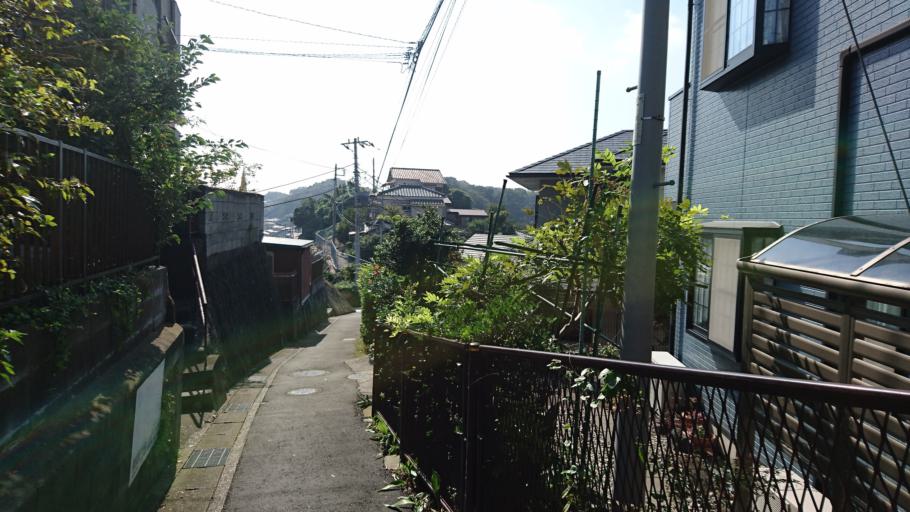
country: JP
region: Kanagawa
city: Yokosuka
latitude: 35.2691
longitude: 139.6745
